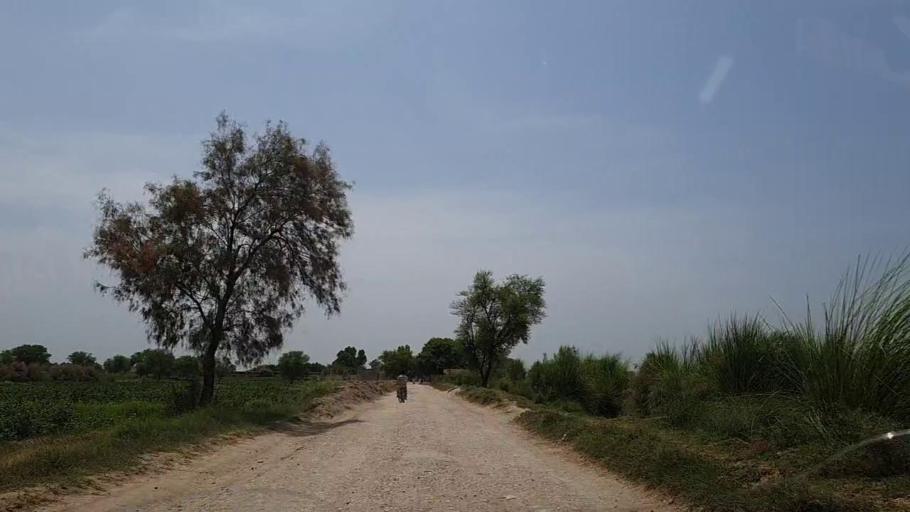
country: PK
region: Sindh
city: Khanpur
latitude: 27.8543
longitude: 69.4863
